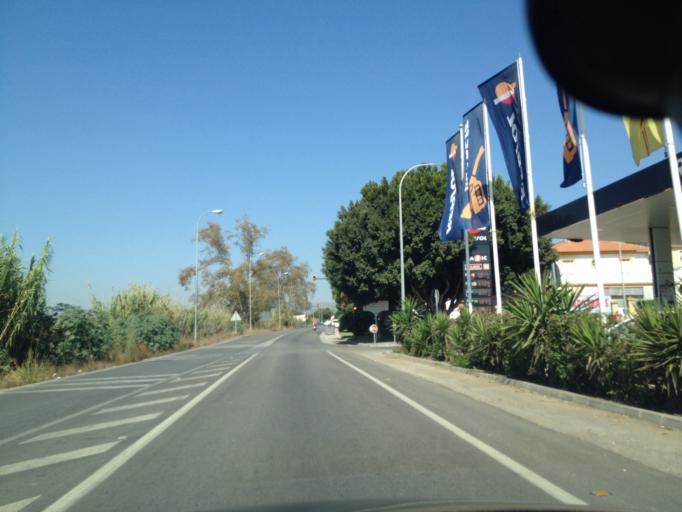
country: ES
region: Andalusia
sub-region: Provincia de Malaga
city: Alhaurin de la Torre
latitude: 36.7195
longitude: -4.5336
